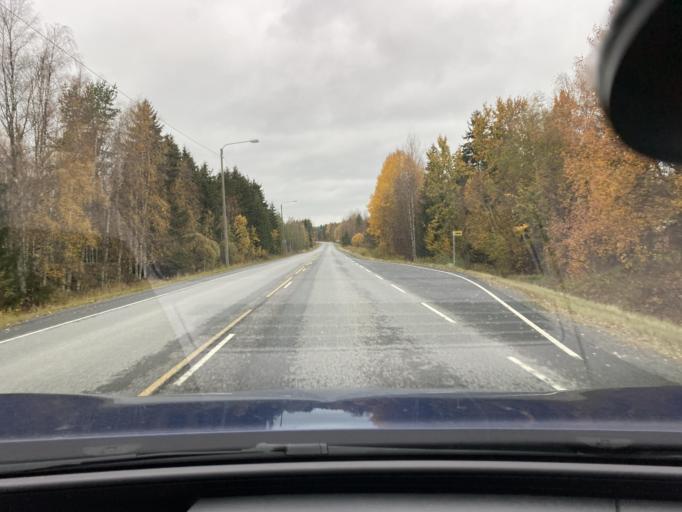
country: FI
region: Satakunta
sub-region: Rauma
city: Rauma
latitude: 61.1303
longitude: 21.6014
